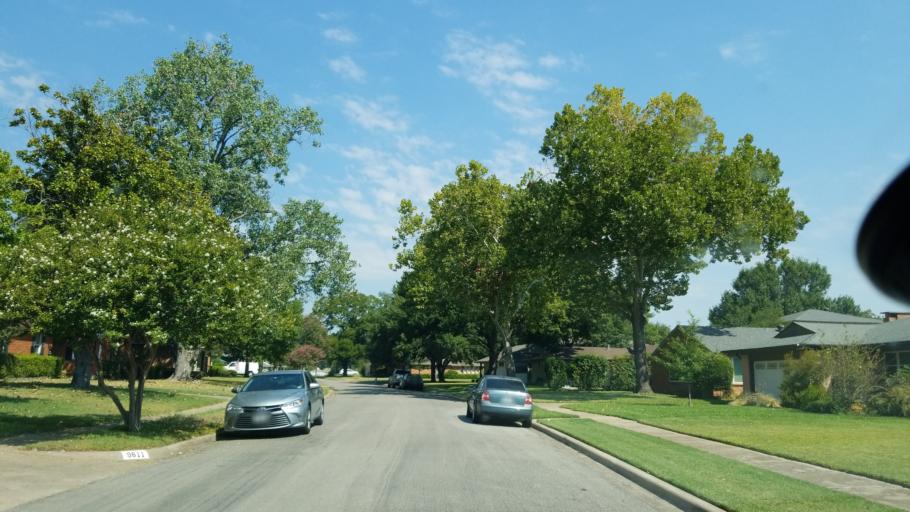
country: US
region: Texas
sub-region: Dallas County
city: Garland
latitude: 32.8769
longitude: -96.7035
